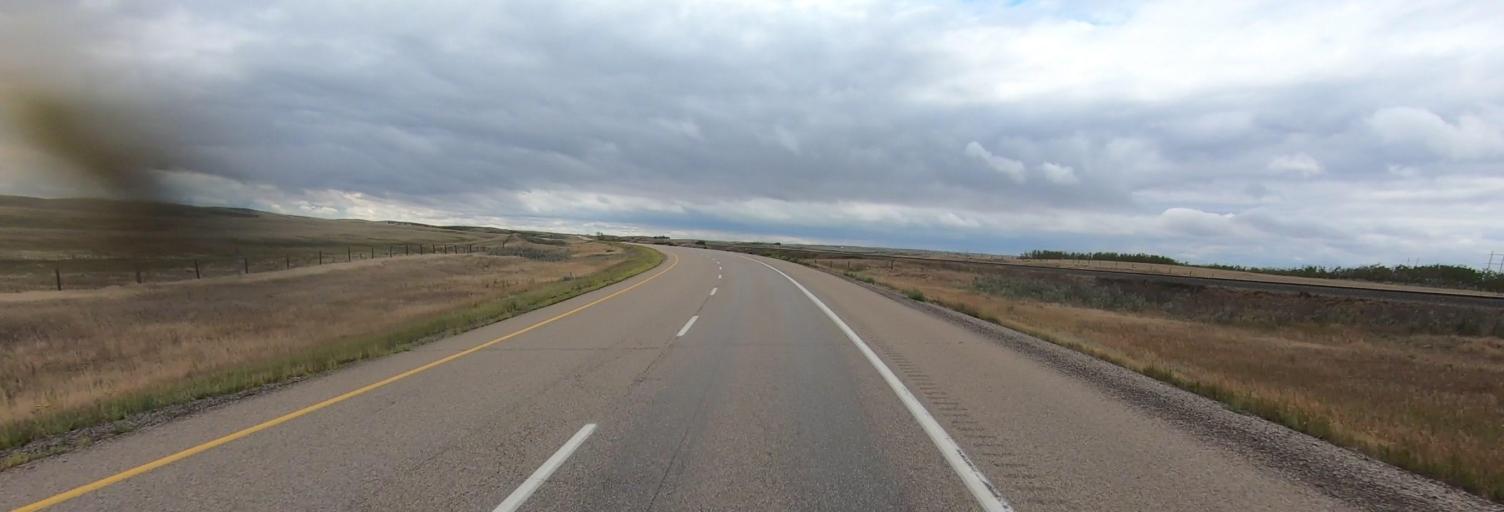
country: CA
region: Saskatchewan
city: Gravelbourg
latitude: 50.4803
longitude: -106.8455
